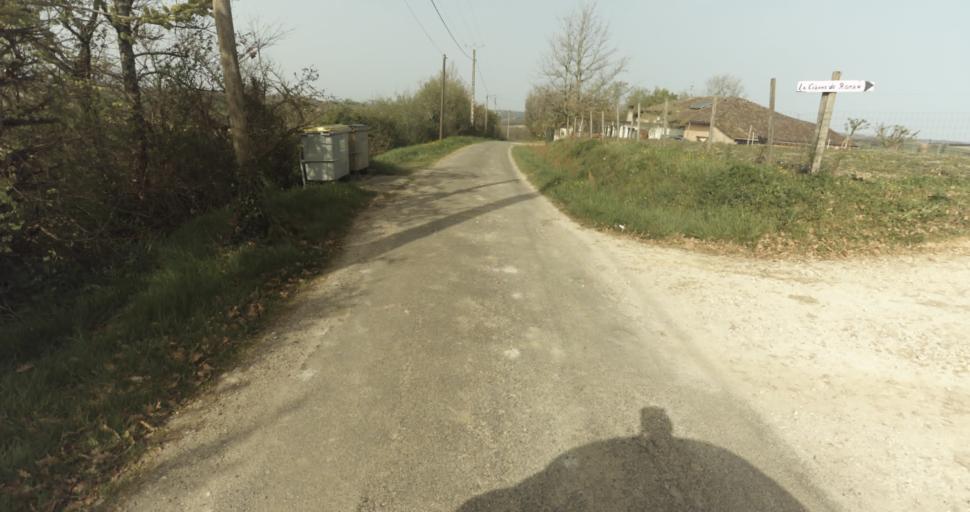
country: FR
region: Midi-Pyrenees
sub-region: Departement du Tarn-et-Garonne
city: Moissac
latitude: 44.1635
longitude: 1.0454
